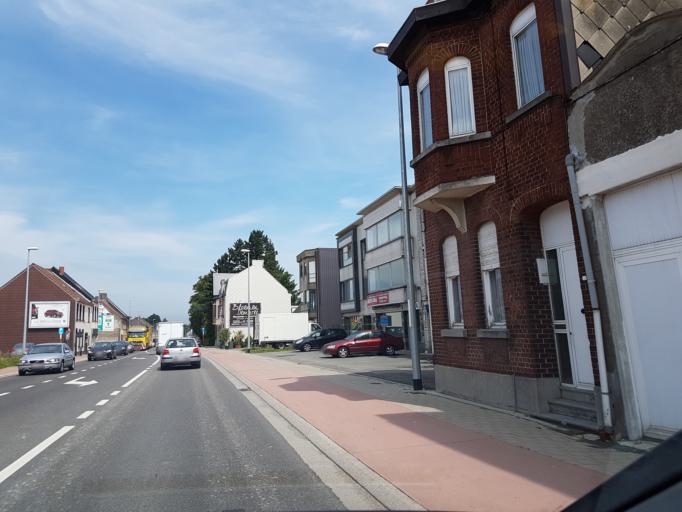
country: BE
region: Flanders
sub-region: Provincie Oost-Vlaanderen
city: Denderleeuw
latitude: 50.9209
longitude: 4.0699
